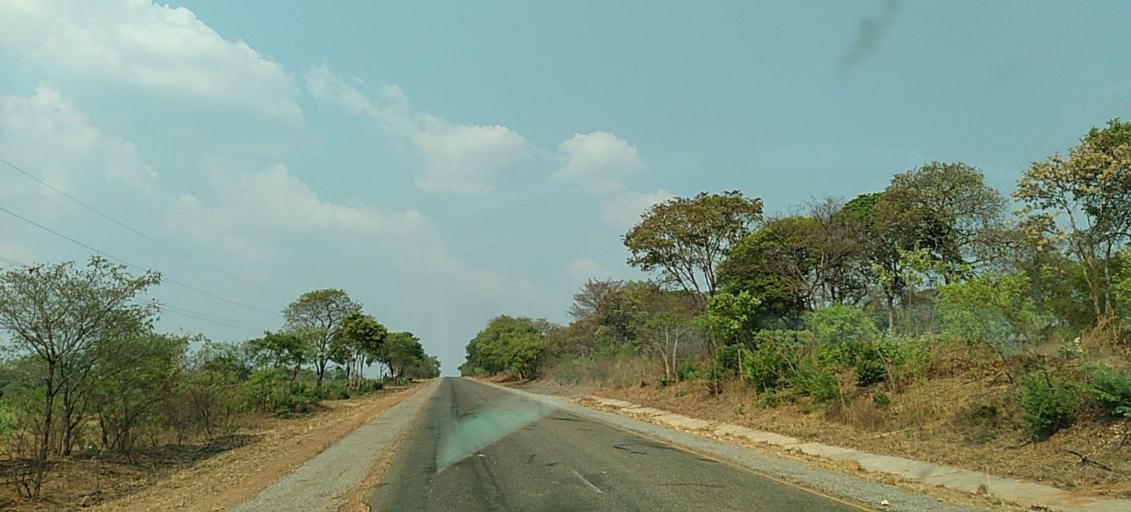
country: ZM
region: North-Western
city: Kabompo
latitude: -13.6184
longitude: 24.1270
